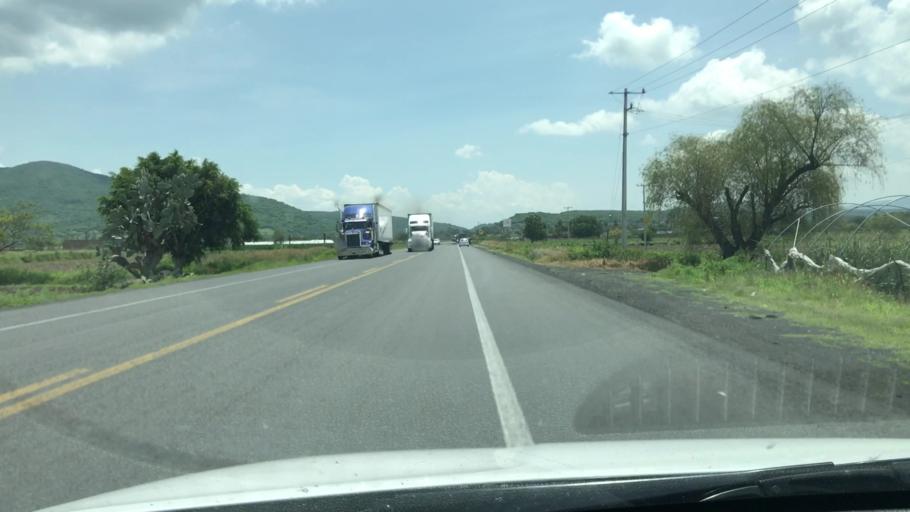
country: MX
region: Michoacan
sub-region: Yurecuaro
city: Yurecuaro
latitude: 20.3270
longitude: -102.2716
